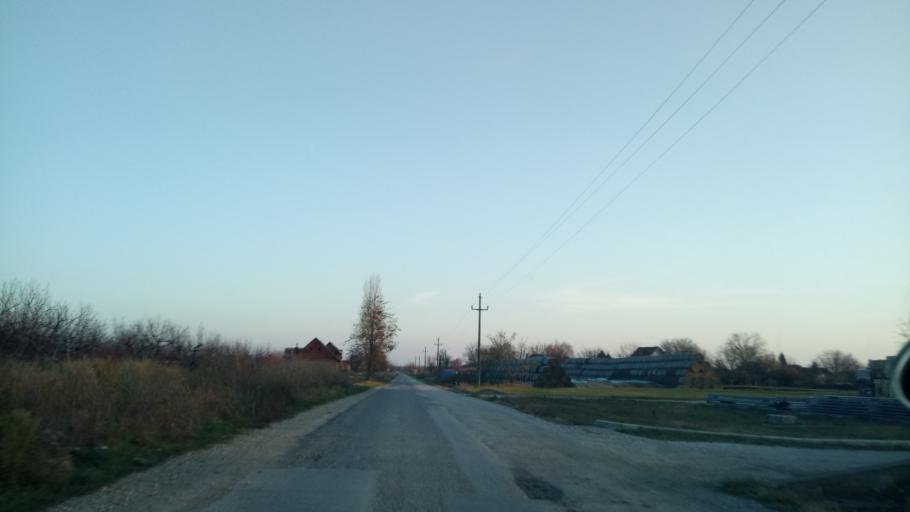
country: RS
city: Novi Slankamen
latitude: 45.1320
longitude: 20.2545
